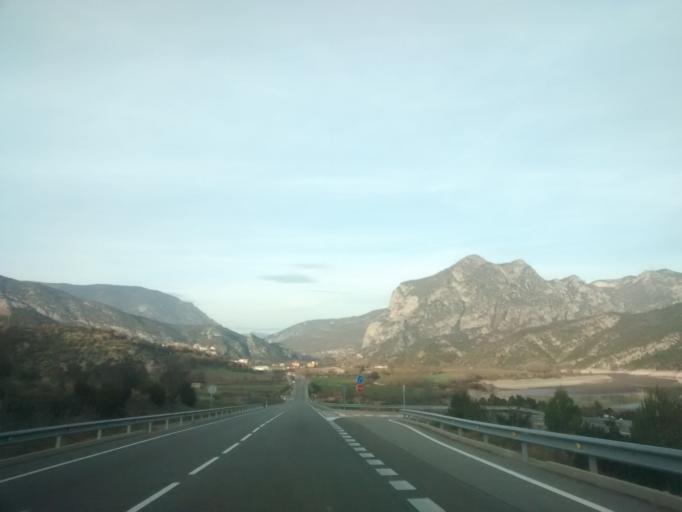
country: ES
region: Catalonia
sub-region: Provincia de Lleida
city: Coll de Nargo
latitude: 42.1580
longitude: 1.3123
